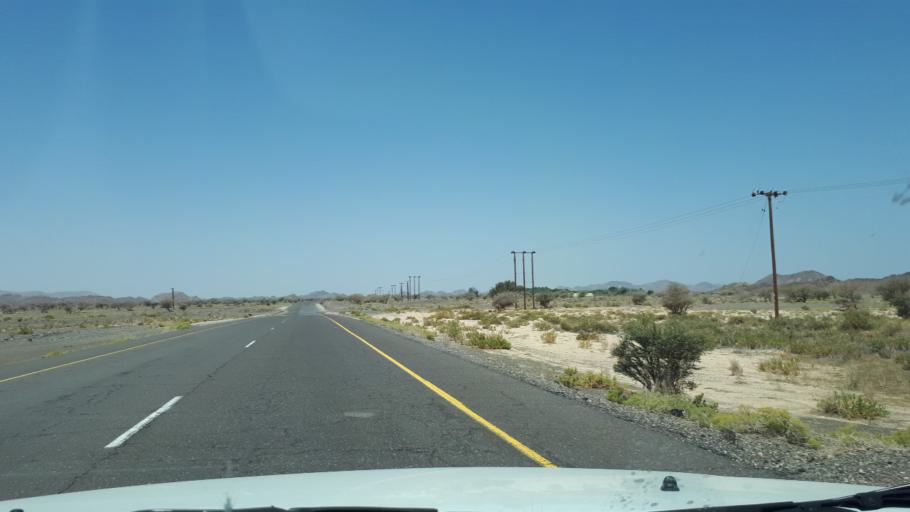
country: OM
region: Ash Sharqiyah
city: Ibra'
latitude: 22.6174
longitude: 58.4302
